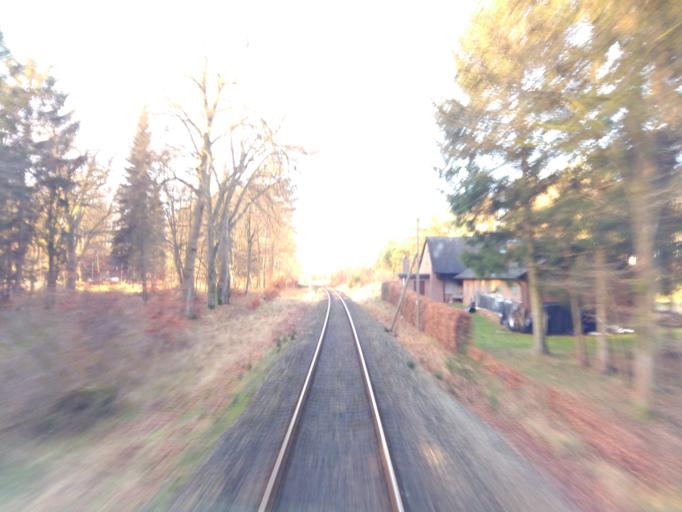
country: DE
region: Lower Saxony
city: Bispingen
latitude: 53.0008
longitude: 9.9993
